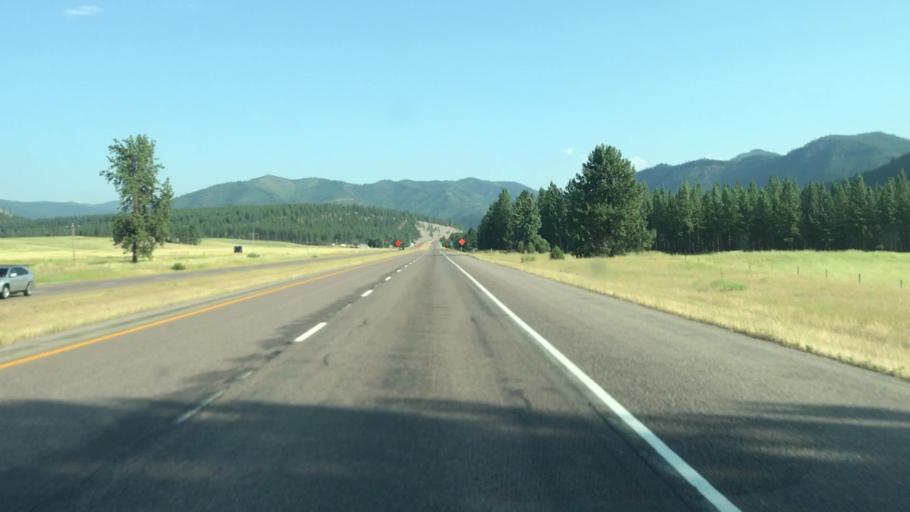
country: US
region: Montana
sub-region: Mineral County
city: Superior
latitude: 47.0387
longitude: -114.7481
